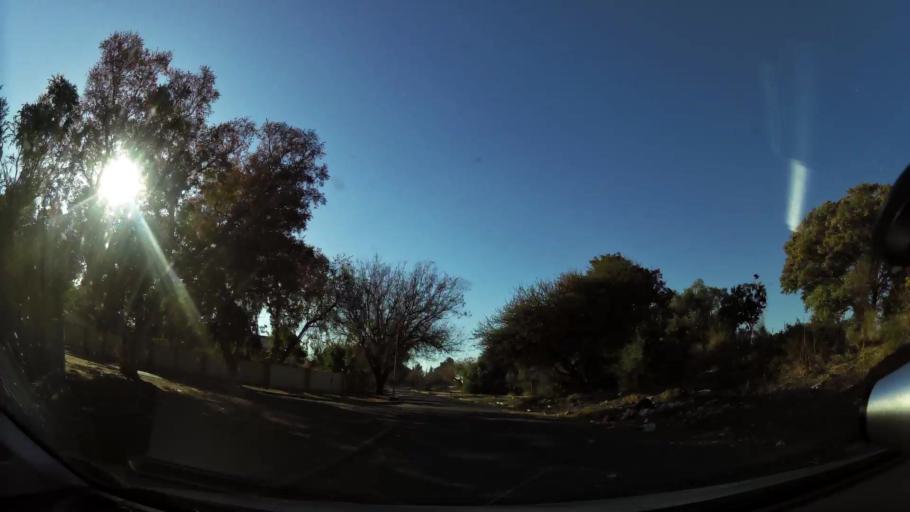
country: ZA
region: Northern Cape
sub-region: Frances Baard District Municipality
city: Kimberley
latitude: -28.7388
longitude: 24.7328
